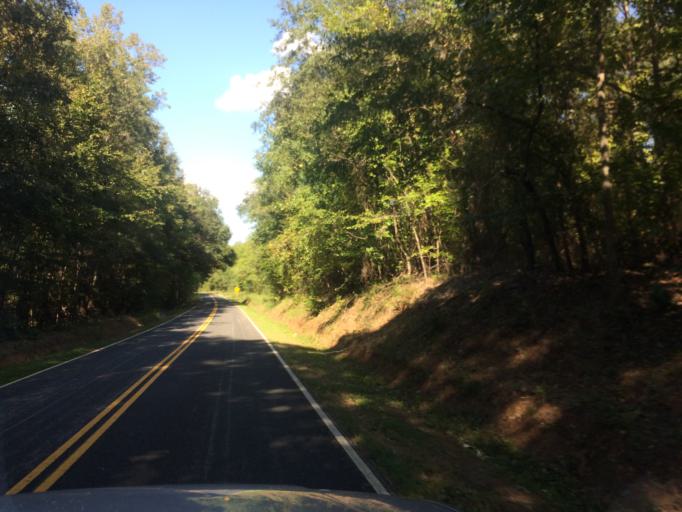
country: US
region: South Carolina
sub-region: Greenwood County
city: Ware Shoals
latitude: 34.4250
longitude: -82.2719
